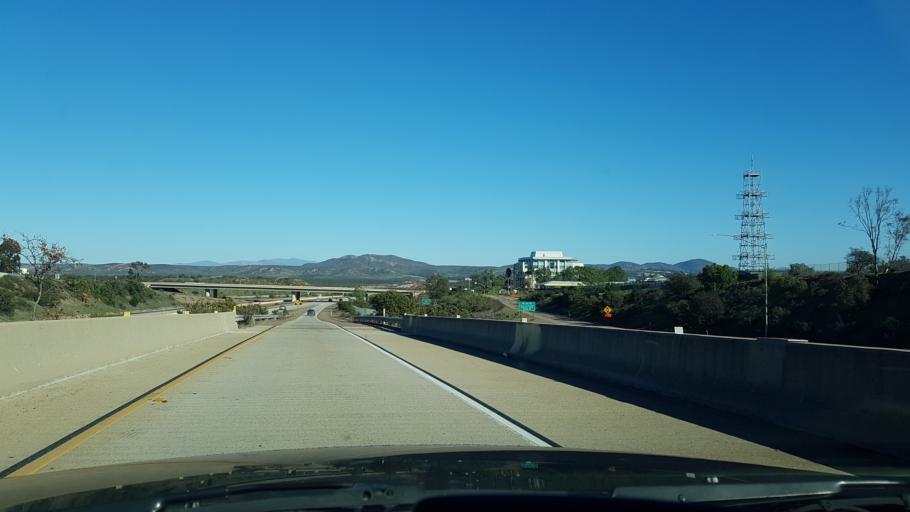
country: US
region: California
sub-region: San Diego County
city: San Diego
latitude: 32.8408
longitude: -117.1323
